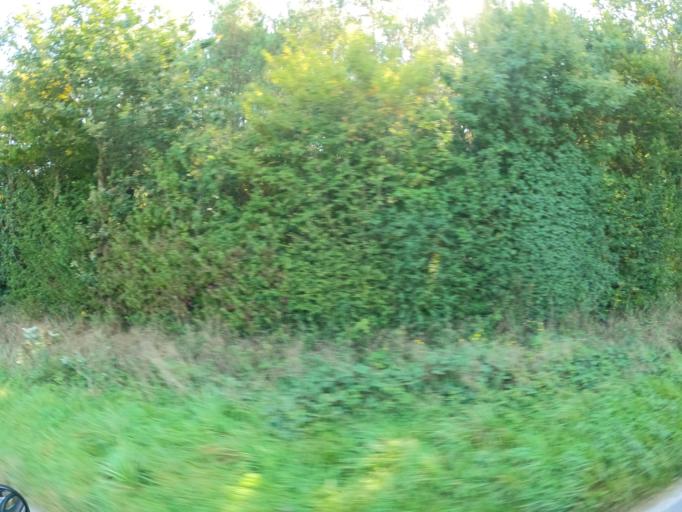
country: FR
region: Pays de la Loire
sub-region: Departement de la Loire-Atlantique
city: La Chevroliere
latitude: 47.0670
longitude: -1.5678
